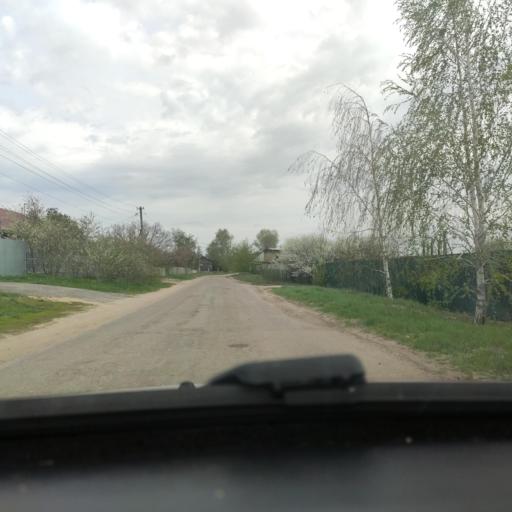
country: RU
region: Voronezj
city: Pridonskoy
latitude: 51.7322
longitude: 39.0576
